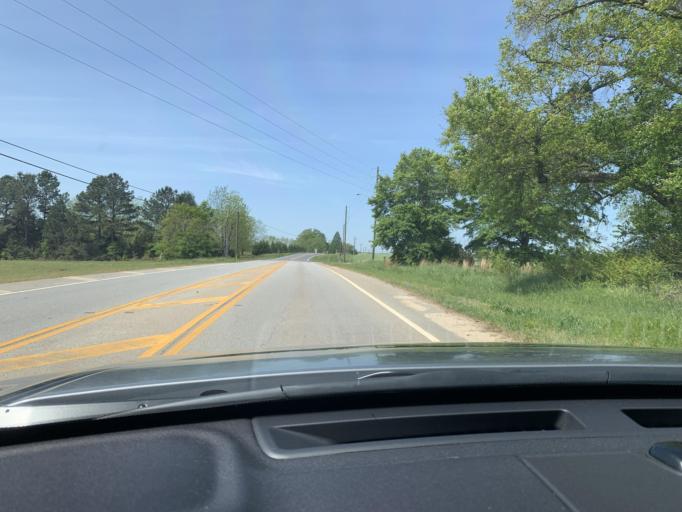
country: US
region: Georgia
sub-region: Oconee County
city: Watkinsville
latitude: 33.8885
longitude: -83.4156
